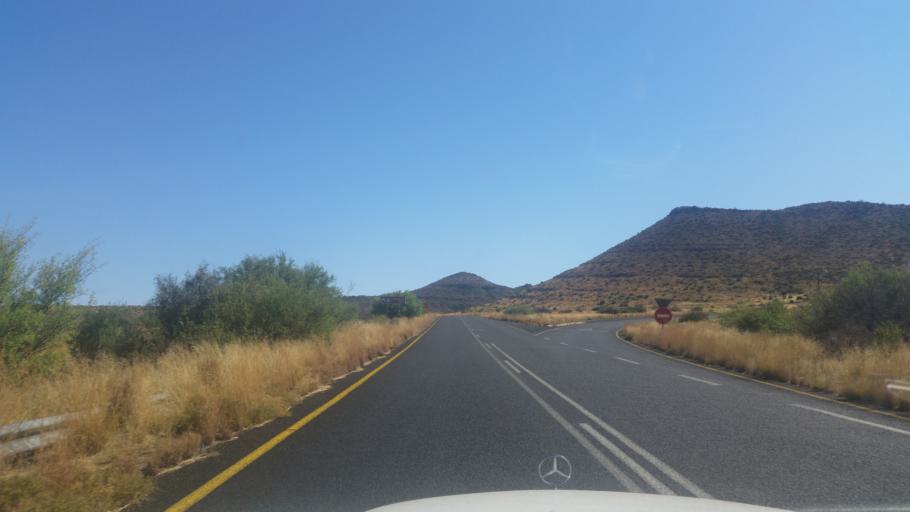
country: ZA
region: Orange Free State
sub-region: Xhariep District Municipality
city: Trompsburg
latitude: -30.4789
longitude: 25.9996
